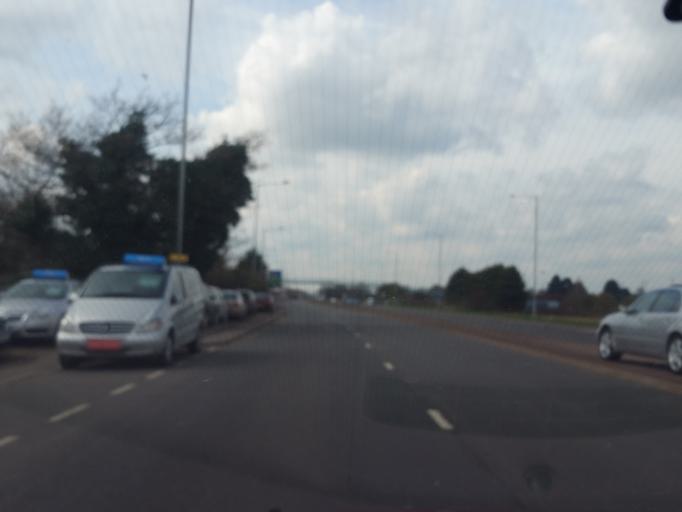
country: GB
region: England
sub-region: Greater London
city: Feltham
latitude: 51.4464
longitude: -0.4589
